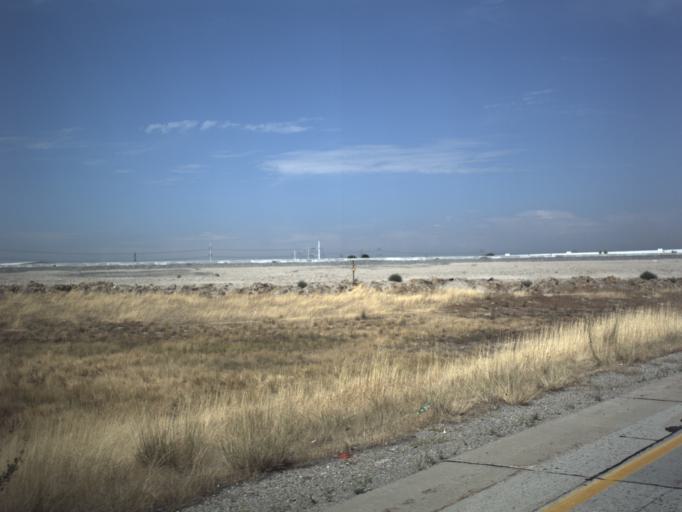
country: US
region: Utah
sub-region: Salt Lake County
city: Taylorsville
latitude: 40.7272
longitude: -111.9493
